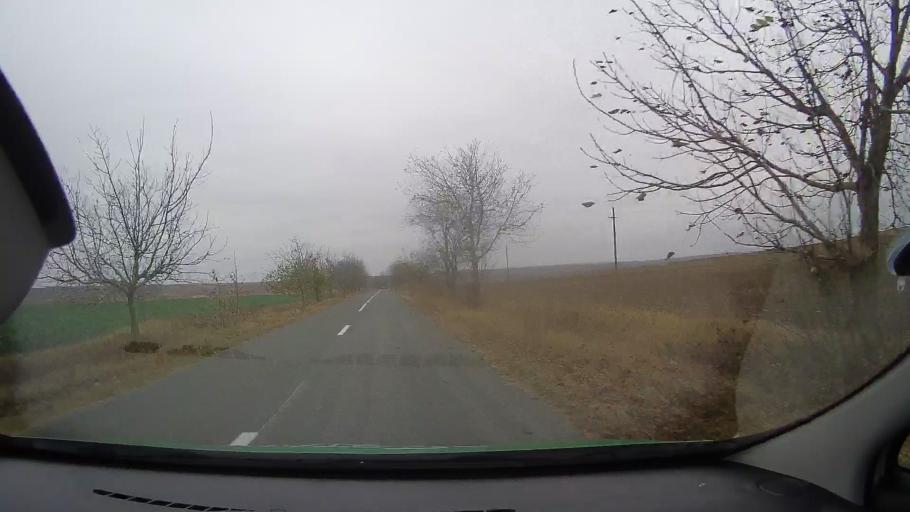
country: RO
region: Constanta
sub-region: Comuna Targusor
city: Targusor
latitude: 44.4815
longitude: 28.3720
